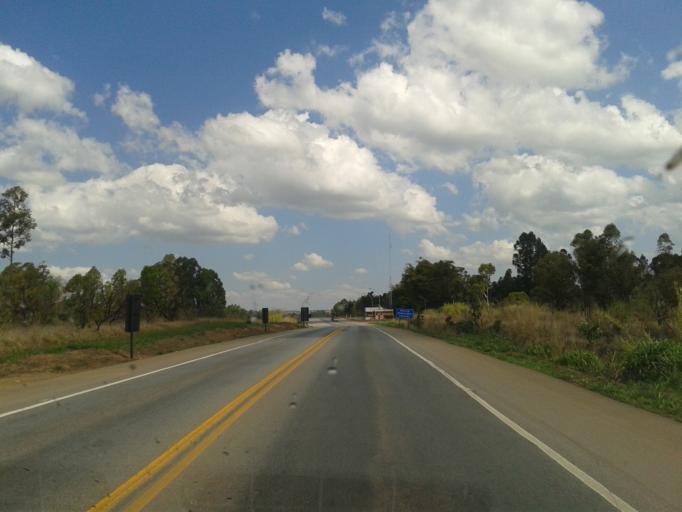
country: BR
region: Minas Gerais
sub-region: Campos Altos
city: Campos Altos
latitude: -19.6738
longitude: -46.0436
